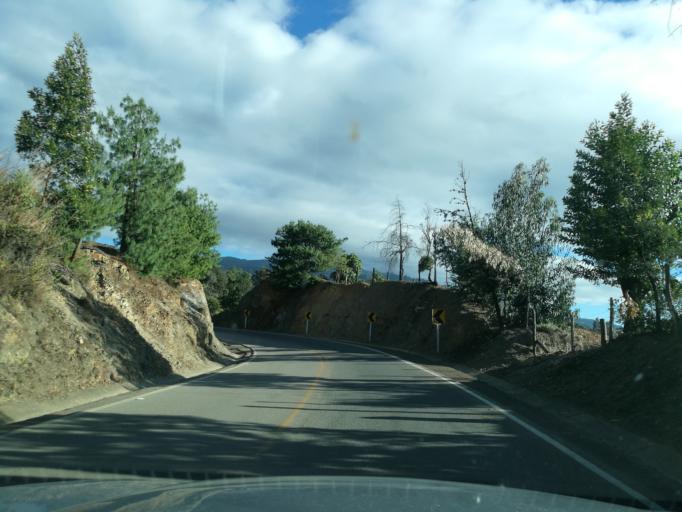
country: CO
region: Boyaca
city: Raquira
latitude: 5.5665
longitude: -73.6707
